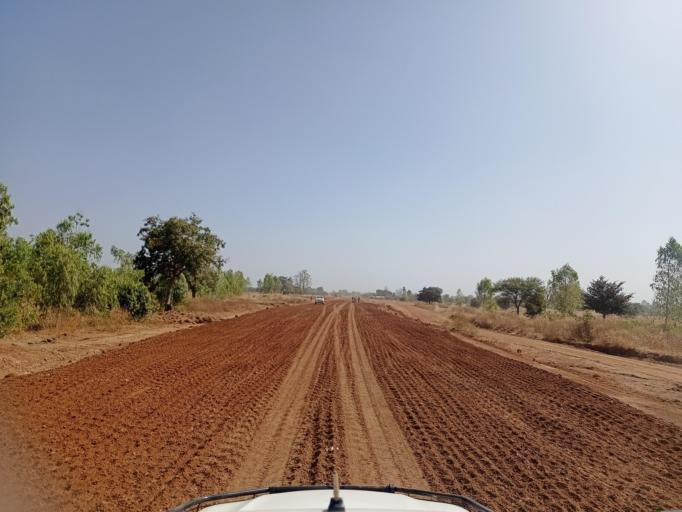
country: BF
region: Centre-Est
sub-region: Province du Boulgou
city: Garango
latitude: 11.5019
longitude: -0.5035
